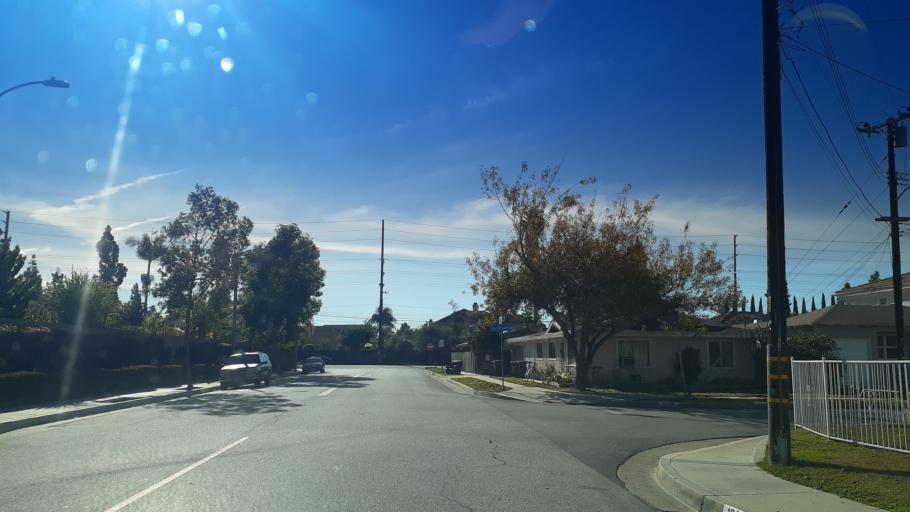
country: US
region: California
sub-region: Los Angeles County
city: Cerritos
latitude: 33.8544
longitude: -118.0689
